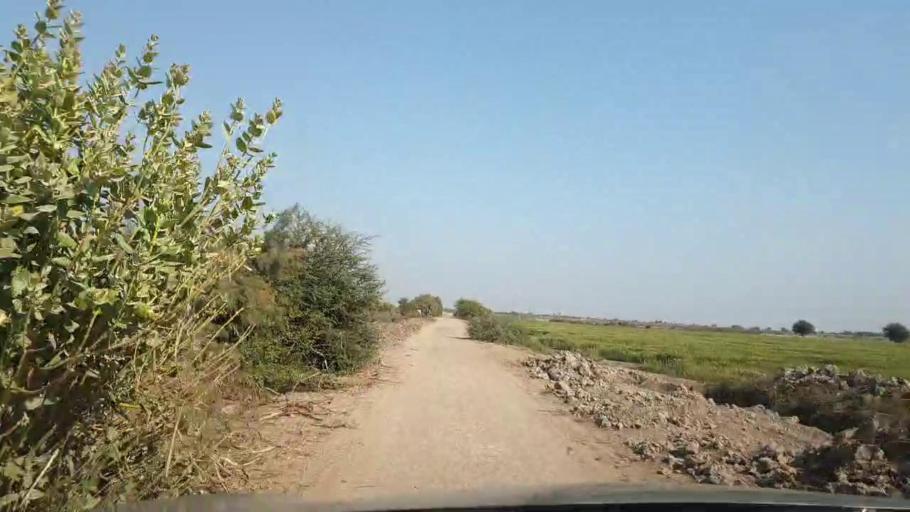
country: PK
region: Sindh
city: Berani
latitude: 25.6223
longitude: 68.8341
